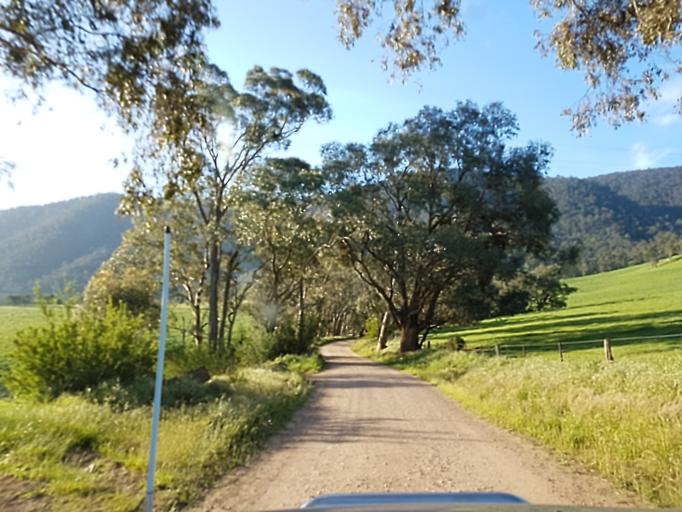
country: AU
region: Victoria
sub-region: East Gippsland
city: Bairnsdale
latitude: -37.4926
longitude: 147.1868
